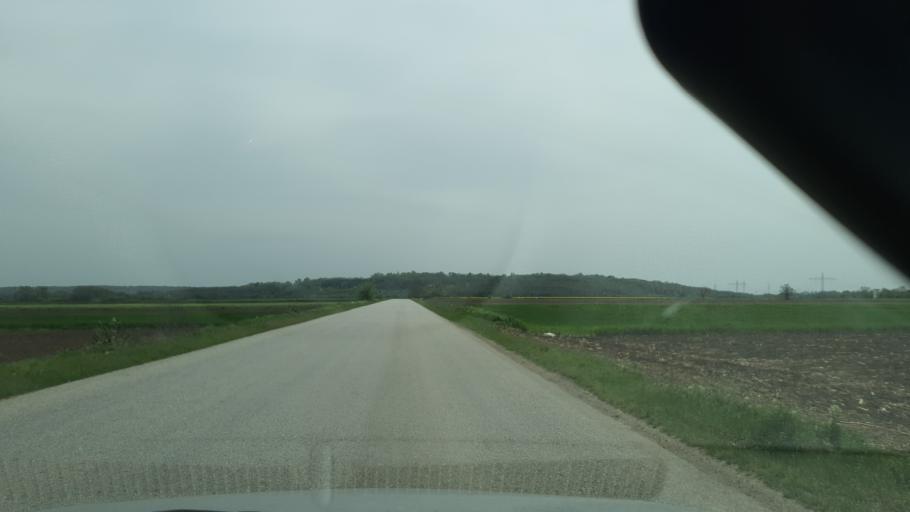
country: RS
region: Central Serbia
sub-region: Branicevski Okrug
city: Pozarevac
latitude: 44.6984
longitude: 21.1591
